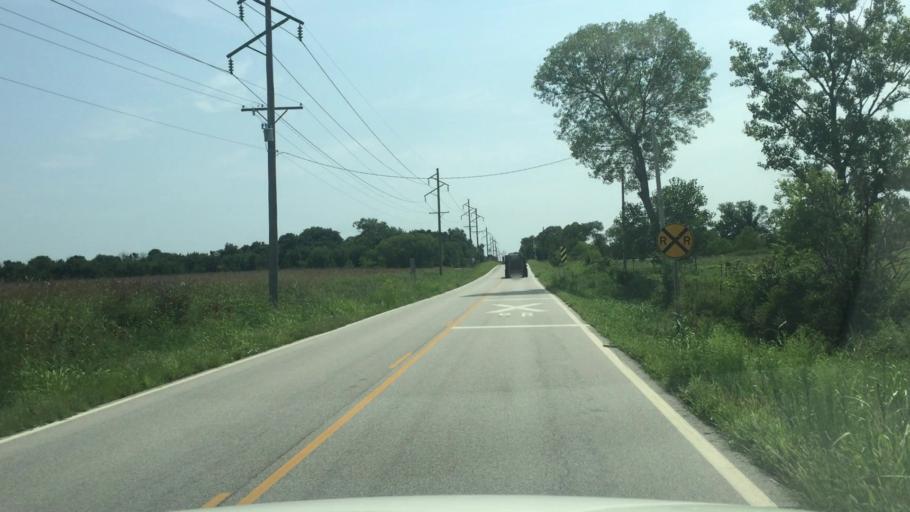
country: US
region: Kansas
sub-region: Montgomery County
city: Cherryvale
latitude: 37.2083
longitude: -95.5681
